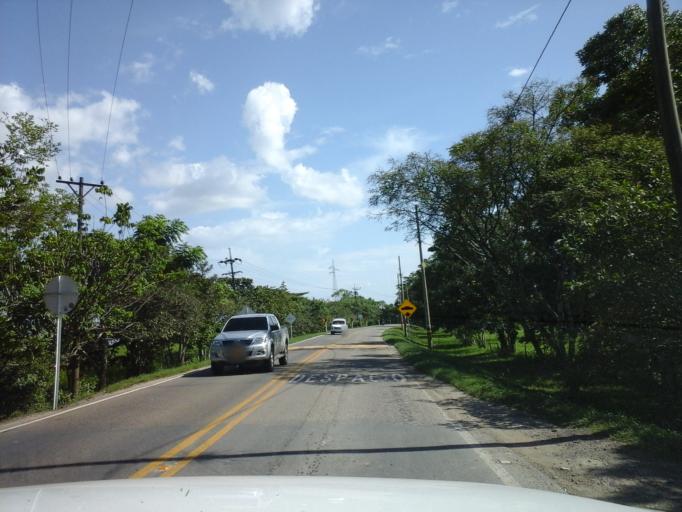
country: CO
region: Meta
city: Puerto Lopez
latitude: 4.1010
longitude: -72.9380
